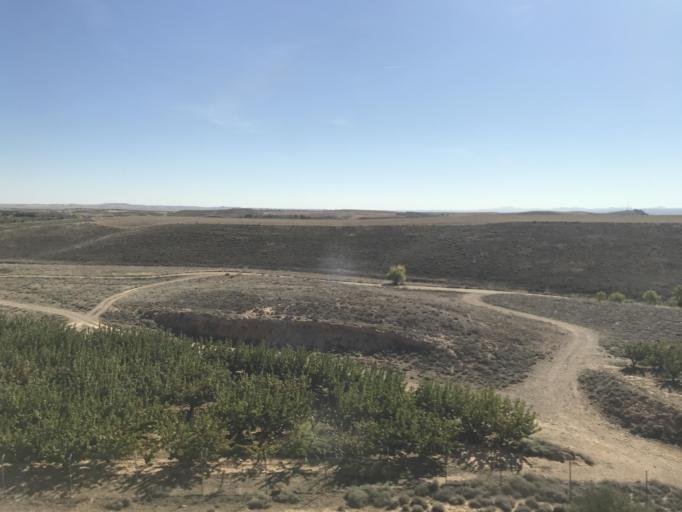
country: ES
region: Aragon
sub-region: Provincia de Zaragoza
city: Calatorao
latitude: 41.5468
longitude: -1.3471
